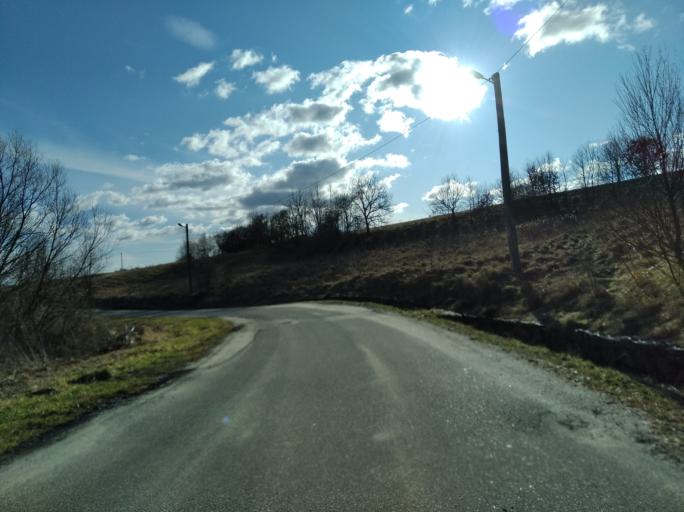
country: PL
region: Subcarpathian Voivodeship
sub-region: Powiat strzyzowski
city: Wisniowa
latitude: 49.8992
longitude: 21.7032
